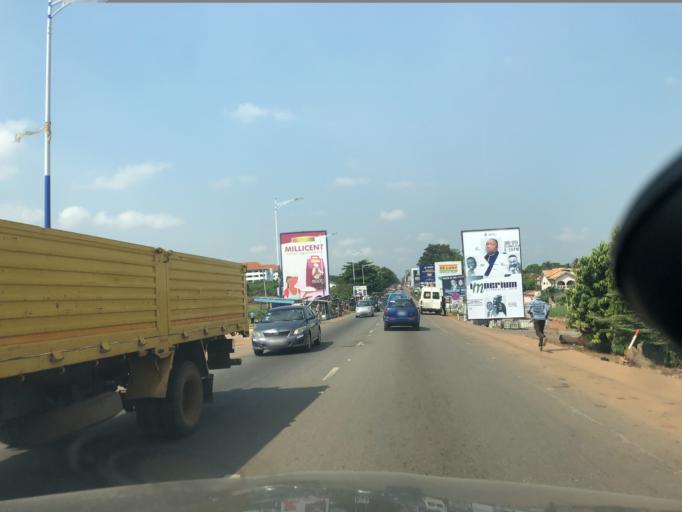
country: GH
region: Greater Accra
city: Medina Estates
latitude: 5.6673
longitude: -0.1785
